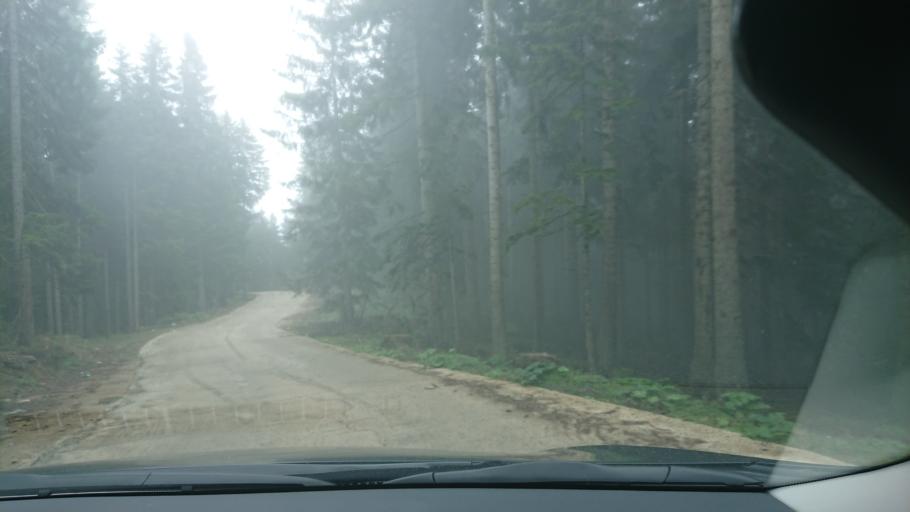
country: TR
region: Gumushane
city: Kurtun
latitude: 40.6645
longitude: 39.0142
